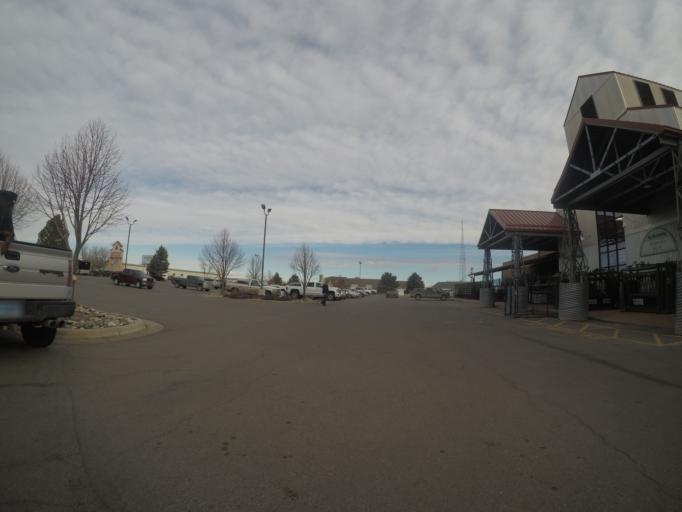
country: US
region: Montana
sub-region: Yellowstone County
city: Billings
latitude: 45.7458
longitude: -108.5815
